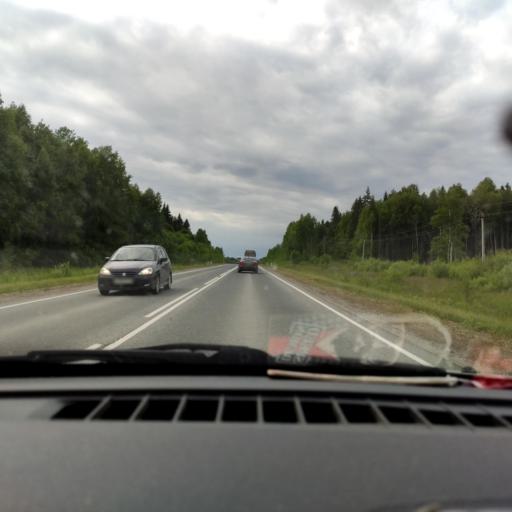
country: RU
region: Perm
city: Verkhnechusovskiye Gorodki
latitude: 58.2683
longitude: 56.9557
